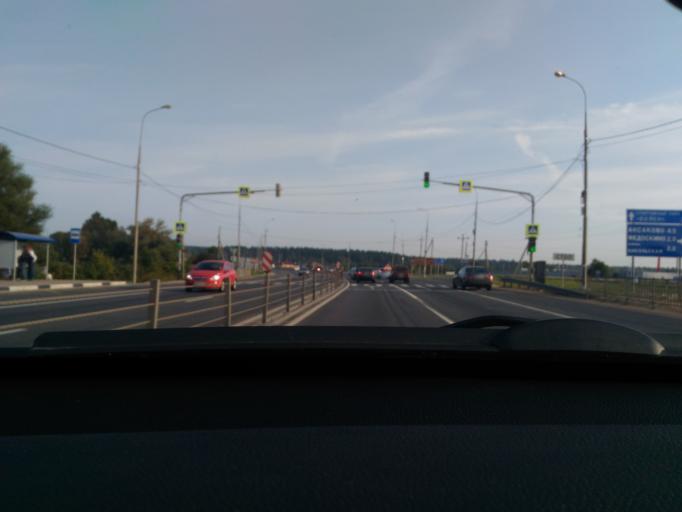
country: RU
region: Moskovskaya
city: Marfino
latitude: 56.0458
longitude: 37.5403
